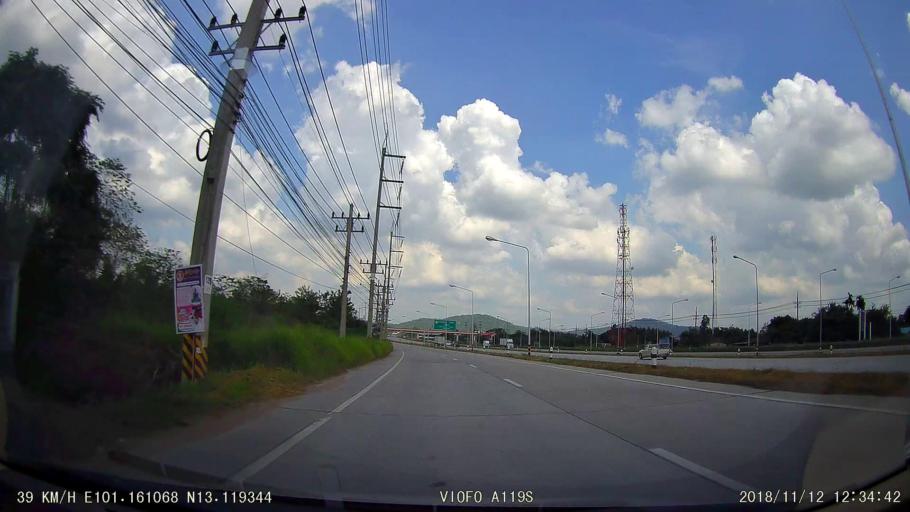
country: TH
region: Rayong
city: Pluak Daeng
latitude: 13.1194
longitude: 101.1611
